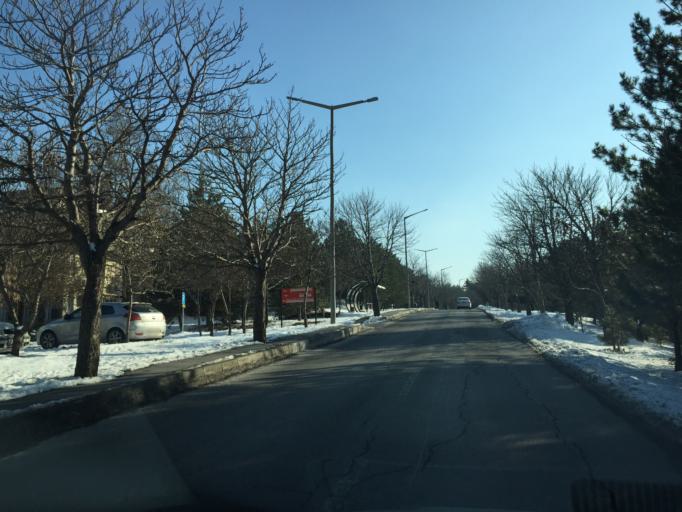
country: TR
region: Ankara
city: Ankara
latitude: 39.8906
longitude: 32.7813
